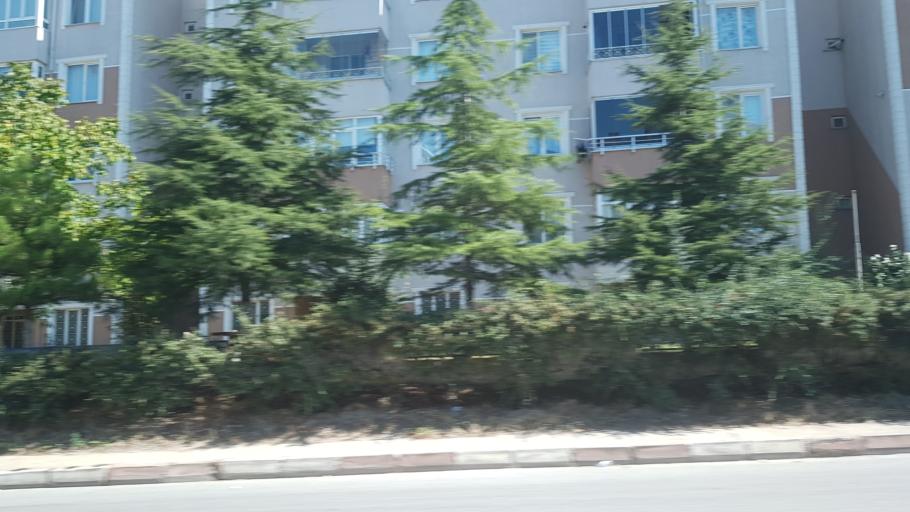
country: TR
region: Kirklareli
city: Kirklareli
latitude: 41.7477
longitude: 27.2197
